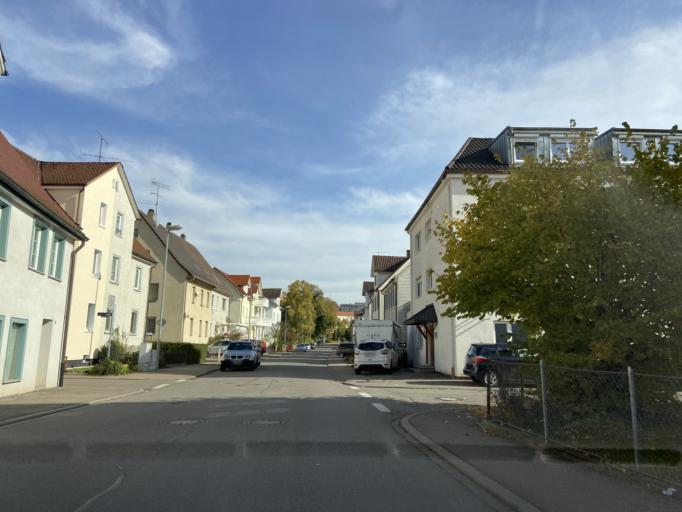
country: DE
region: Baden-Wuerttemberg
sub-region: Tuebingen Region
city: Sigmaringen
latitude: 48.0915
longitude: 9.2103
